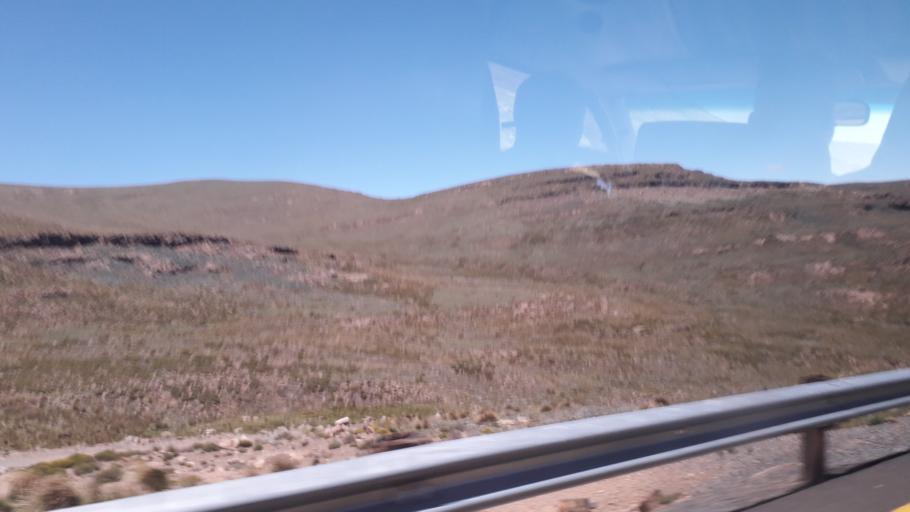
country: ZA
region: Orange Free State
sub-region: Thabo Mofutsanyana District Municipality
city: Phuthaditjhaba
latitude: -28.8073
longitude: 28.7011
